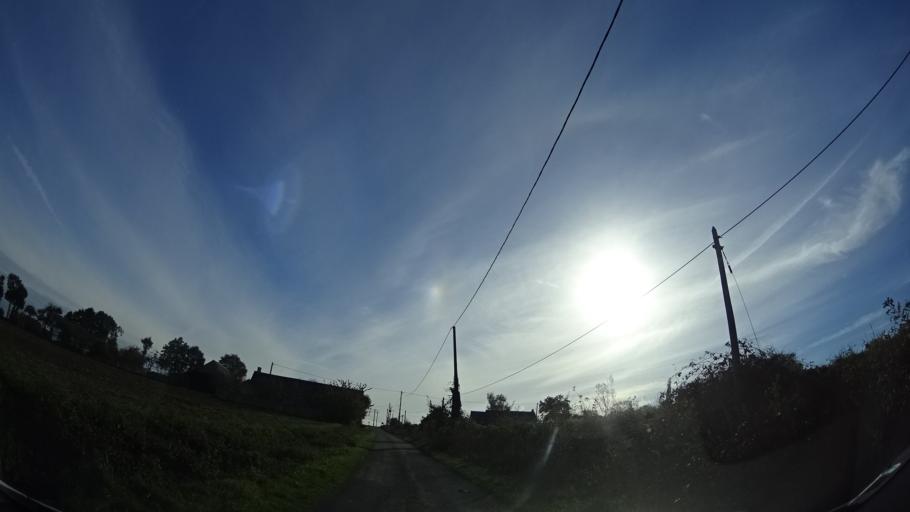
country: FR
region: Brittany
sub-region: Departement d'Ille-et-Vilaine
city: Geveze
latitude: 48.2307
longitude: -1.8268
